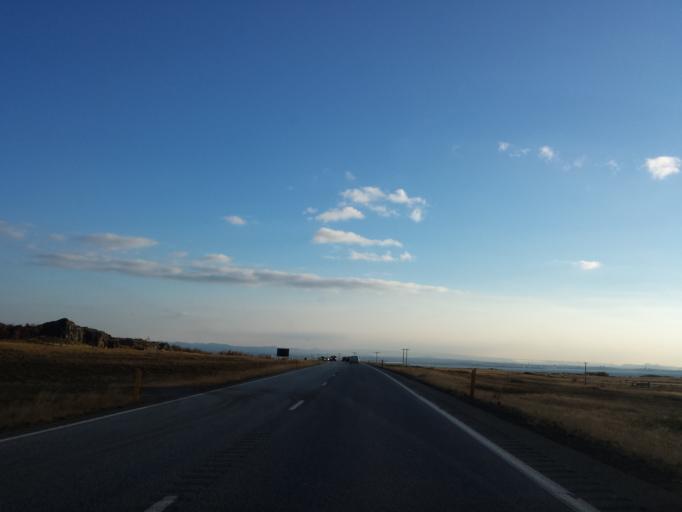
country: IS
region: Capital Region
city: Reykjavik
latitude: 64.2600
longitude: -21.8328
